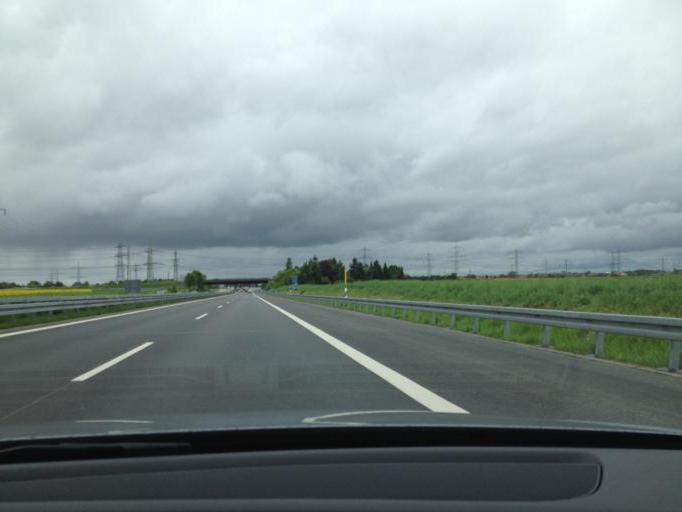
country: DE
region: Baden-Wuerttemberg
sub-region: Karlsruhe Region
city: Ilvesheim
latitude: 49.4563
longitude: 8.5531
